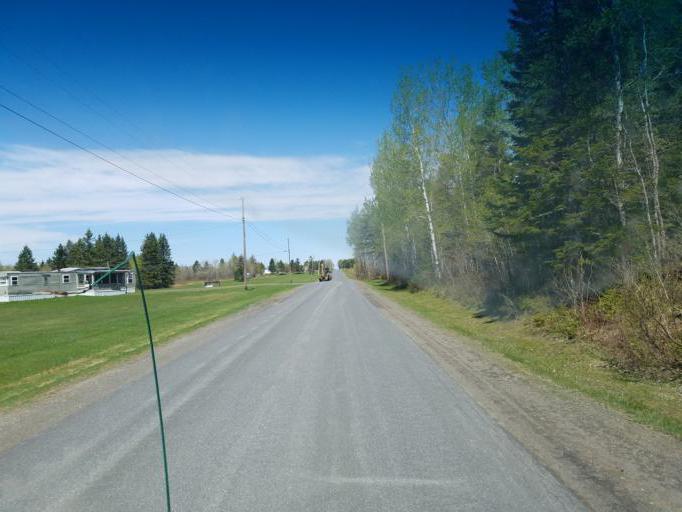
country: US
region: Maine
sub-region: Aroostook County
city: Caribou
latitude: 46.8443
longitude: -68.0703
